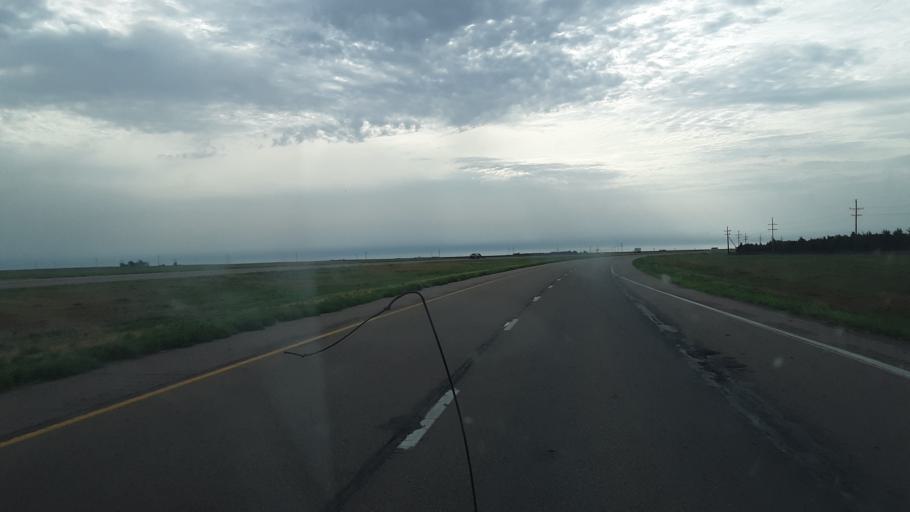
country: US
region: Kansas
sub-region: Finney County
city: Garden City
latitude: 37.9604
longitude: -100.7467
